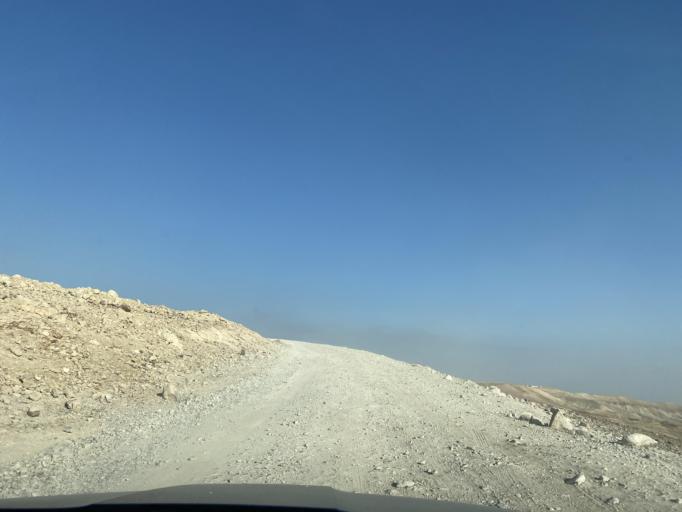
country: PS
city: `Arab ar Rashaydah
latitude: 31.5232
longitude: 35.3001
